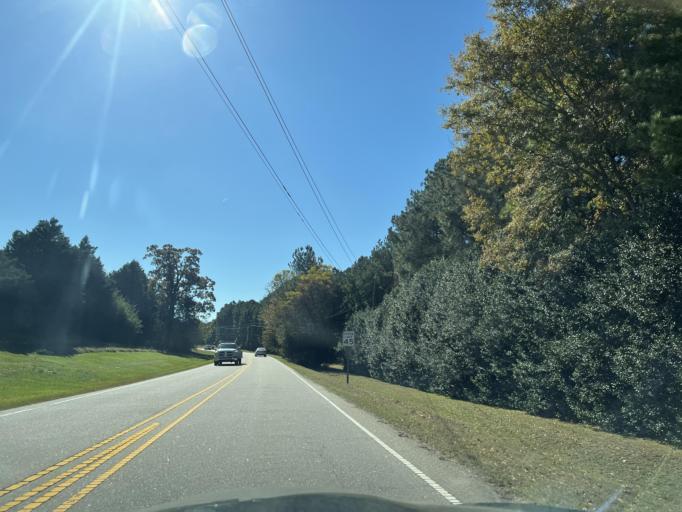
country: US
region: North Carolina
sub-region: Wake County
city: Garner
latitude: 35.7071
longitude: -78.6888
